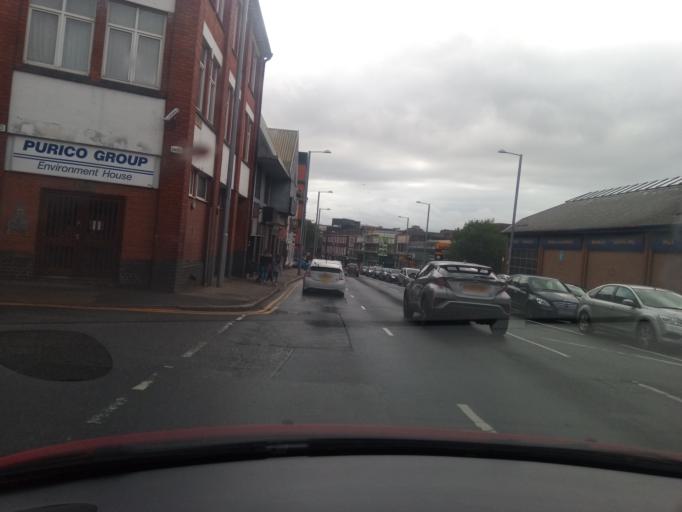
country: GB
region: England
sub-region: Nottingham
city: Nottingham
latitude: 52.9581
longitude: -1.1457
